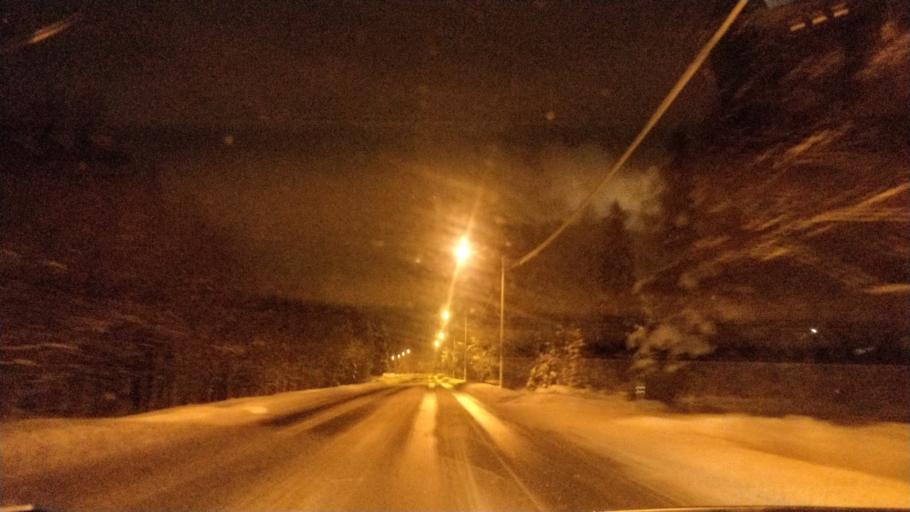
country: FI
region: Lapland
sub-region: Rovaniemi
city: Rovaniemi
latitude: 66.3822
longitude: 25.3784
